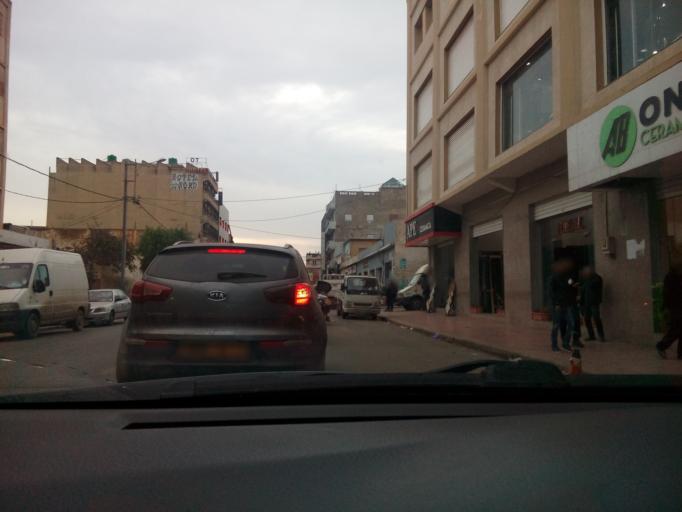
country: DZ
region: Oran
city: Oran
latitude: 35.6868
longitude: -0.6413
